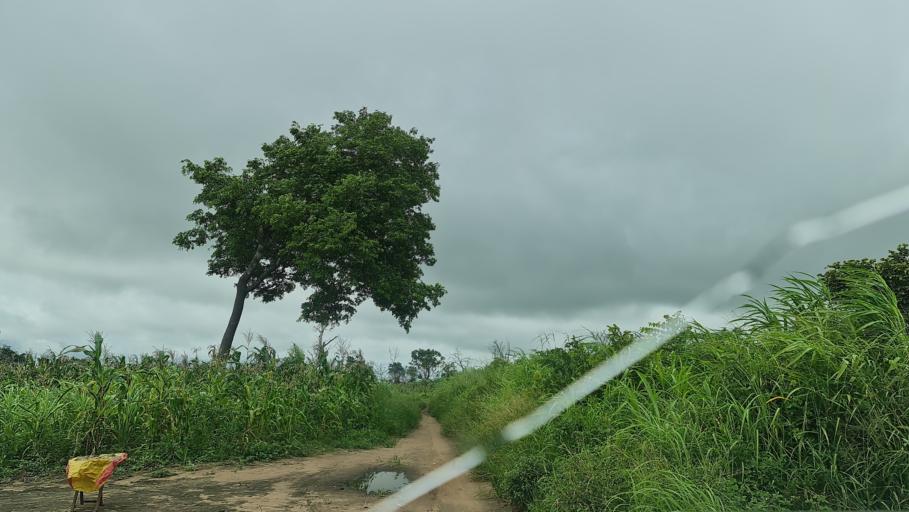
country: MW
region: Southern Region
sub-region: Nsanje District
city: Nsanje
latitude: -17.3396
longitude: 35.7265
